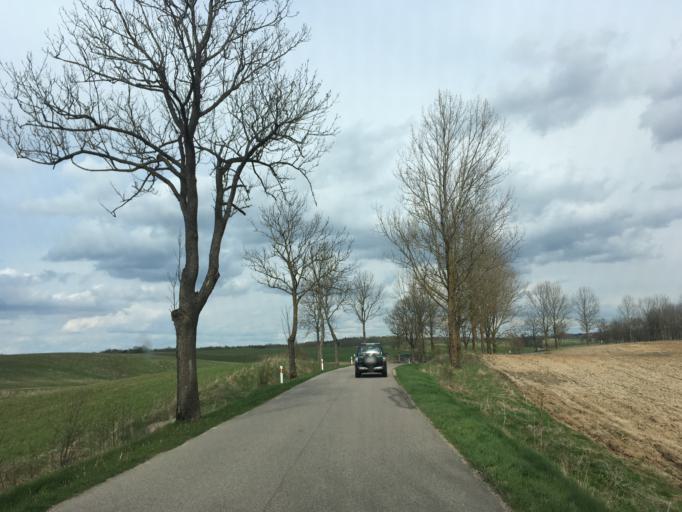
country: PL
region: Podlasie
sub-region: Powiat suwalski
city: Filipow
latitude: 54.3568
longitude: 22.7646
